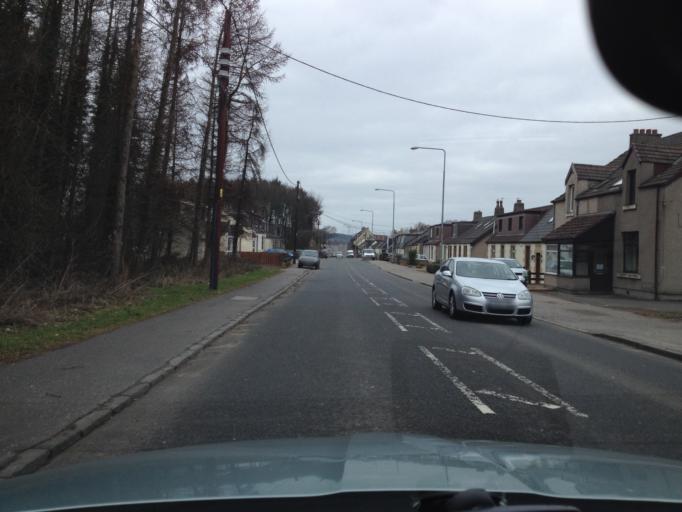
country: GB
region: Scotland
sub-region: West Lothian
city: Livingston
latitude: 55.9131
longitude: -3.4994
